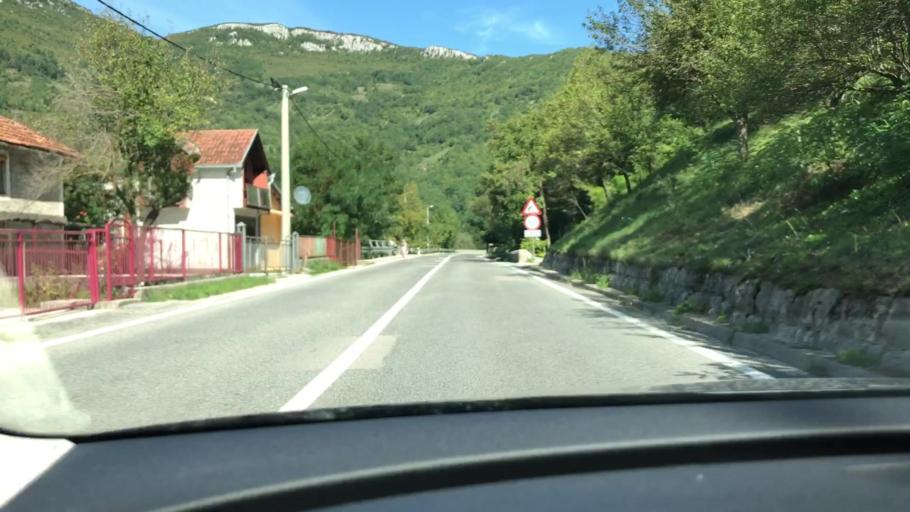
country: BA
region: Federation of Bosnia and Herzegovina
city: Jablanica
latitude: 43.6837
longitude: 17.7874
